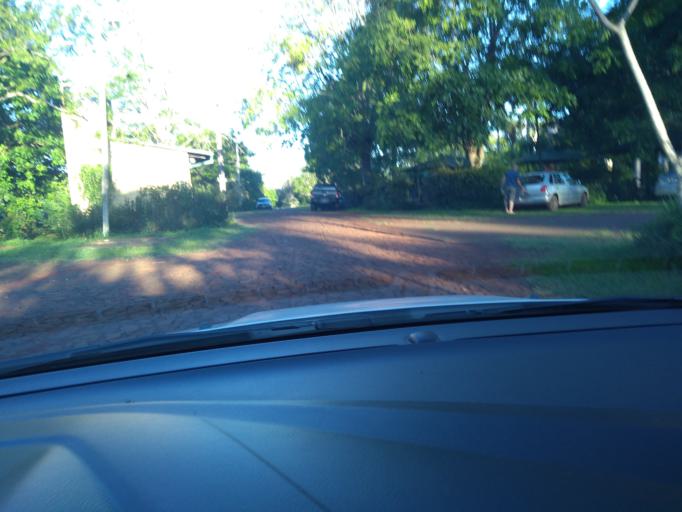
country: AR
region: Misiones
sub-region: Departamento de Obera
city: Obera
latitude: -27.4694
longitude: -55.0842
